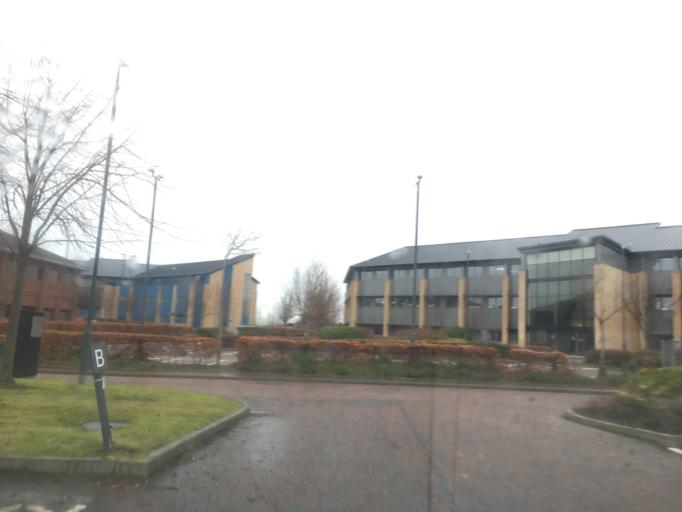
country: GB
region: Scotland
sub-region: Edinburgh
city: Currie
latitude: 55.9331
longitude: -3.3048
